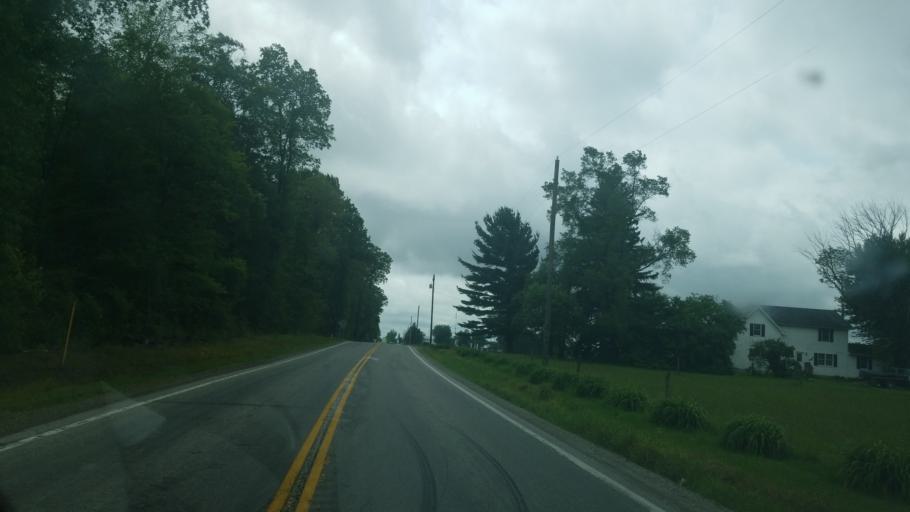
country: US
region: Ohio
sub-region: Crawford County
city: Galion
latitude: 40.7330
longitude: -82.8950
